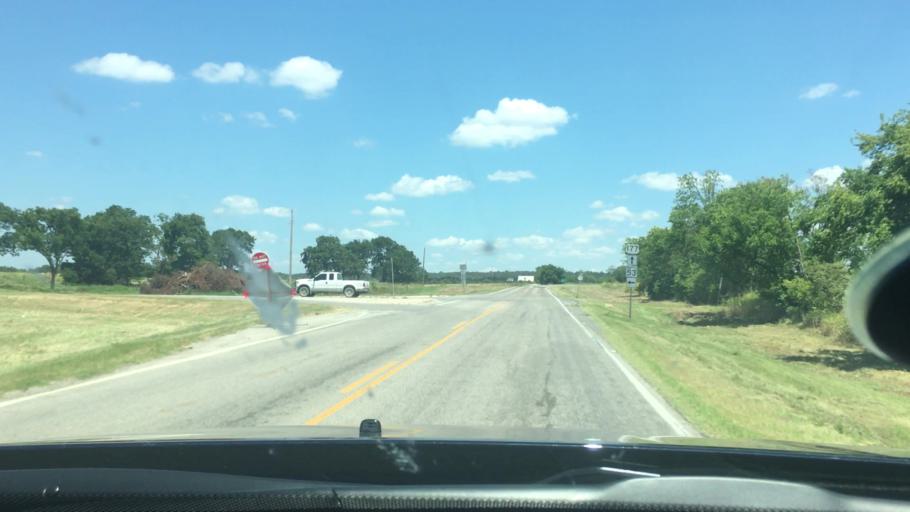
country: US
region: Oklahoma
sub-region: Carter County
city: Dickson
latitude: 34.2883
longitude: -96.9682
